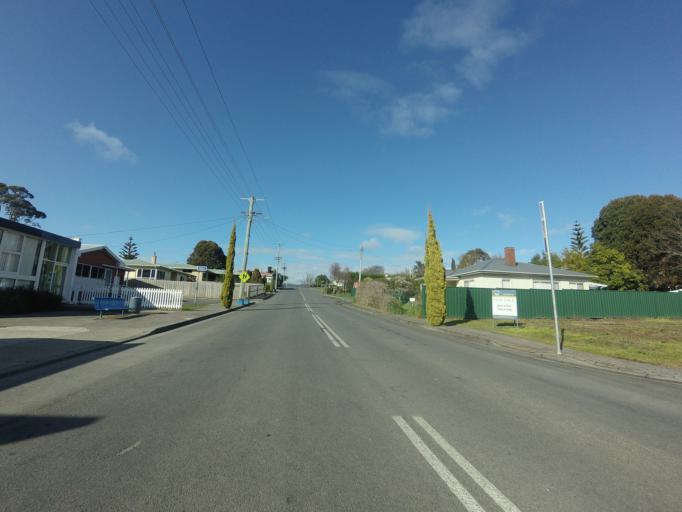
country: AU
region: Tasmania
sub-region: Huon Valley
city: Cygnet
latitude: -43.3124
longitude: 147.0156
